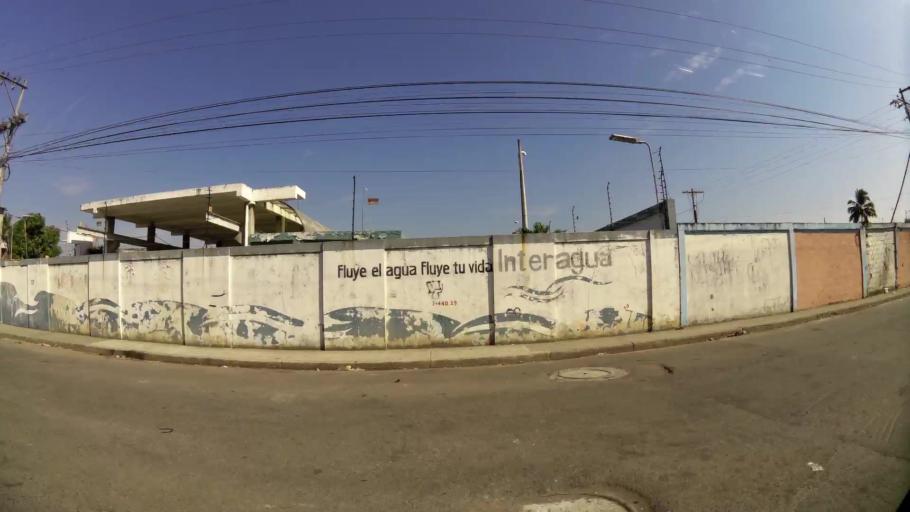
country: EC
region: Guayas
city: Eloy Alfaro
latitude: -2.1031
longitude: -79.9220
